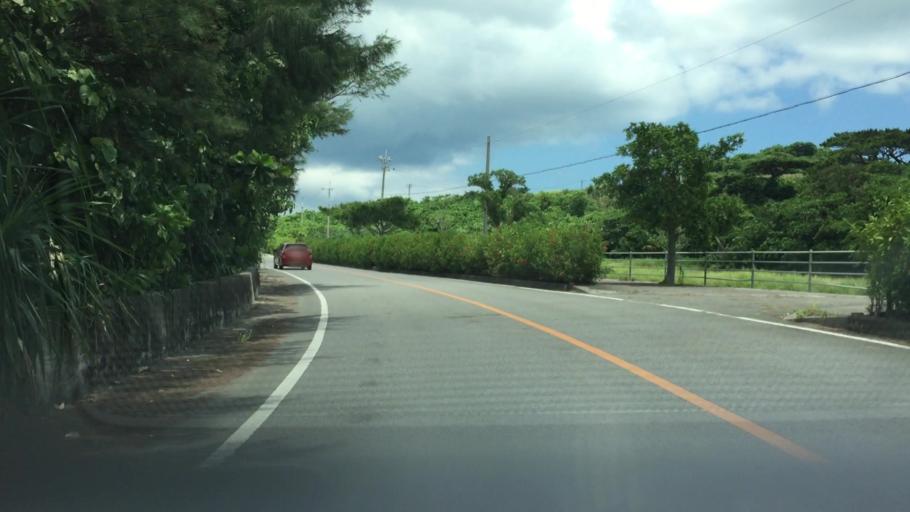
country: JP
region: Okinawa
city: Ishigaki
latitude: 24.4251
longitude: 124.1287
